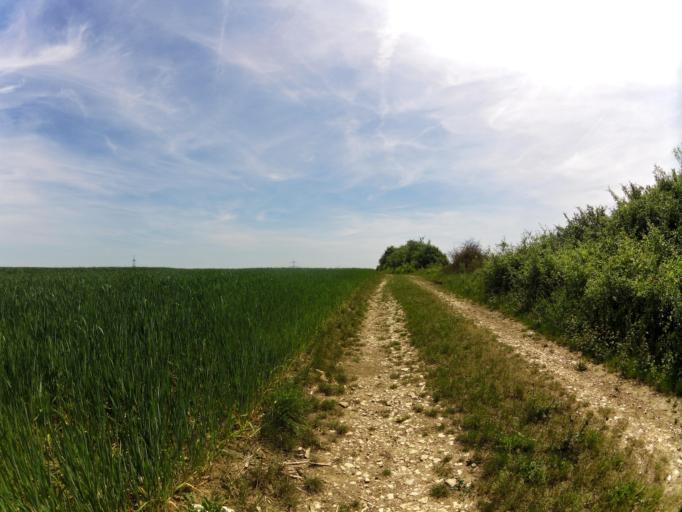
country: DE
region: Bavaria
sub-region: Regierungsbezirk Unterfranken
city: Ochsenfurt
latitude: 49.6678
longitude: 10.0266
